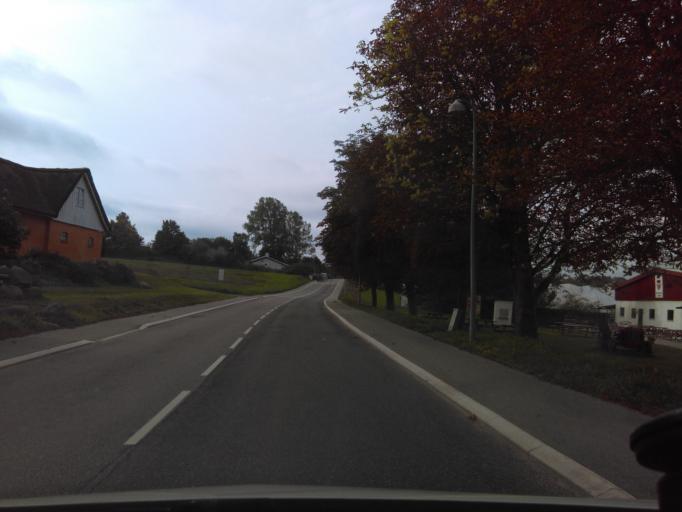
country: DK
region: Capital Region
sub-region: Ballerup Kommune
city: Malov
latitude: 55.7800
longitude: 12.3236
